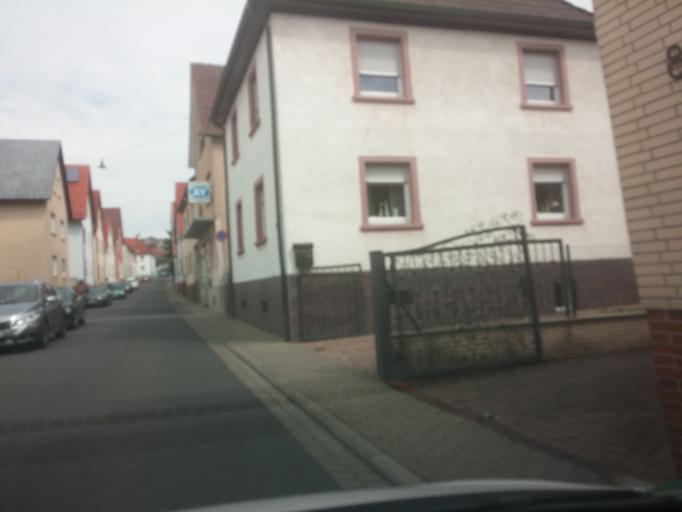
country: DE
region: Bavaria
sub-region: Regierungsbezirk Unterfranken
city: Goldbach
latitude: 49.9993
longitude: 9.1876
